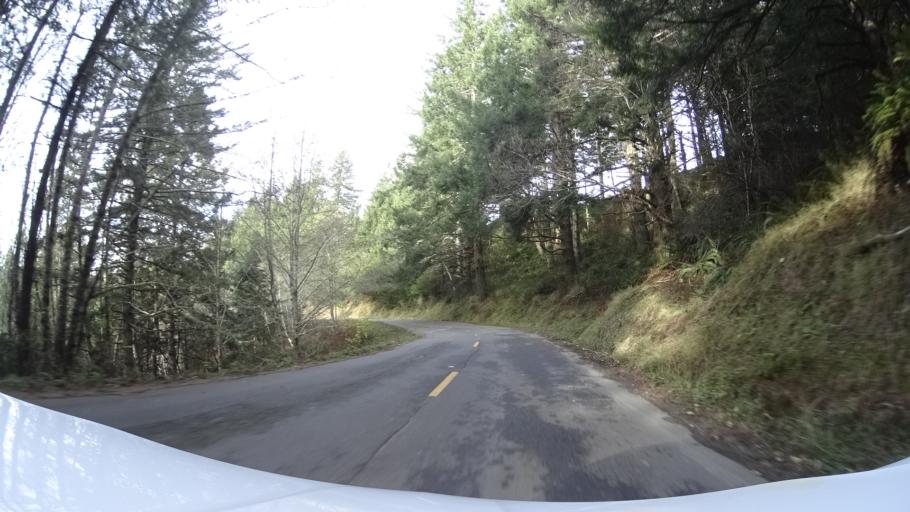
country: US
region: California
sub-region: Humboldt County
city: Ferndale
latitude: 40.5263
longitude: -124.2675
